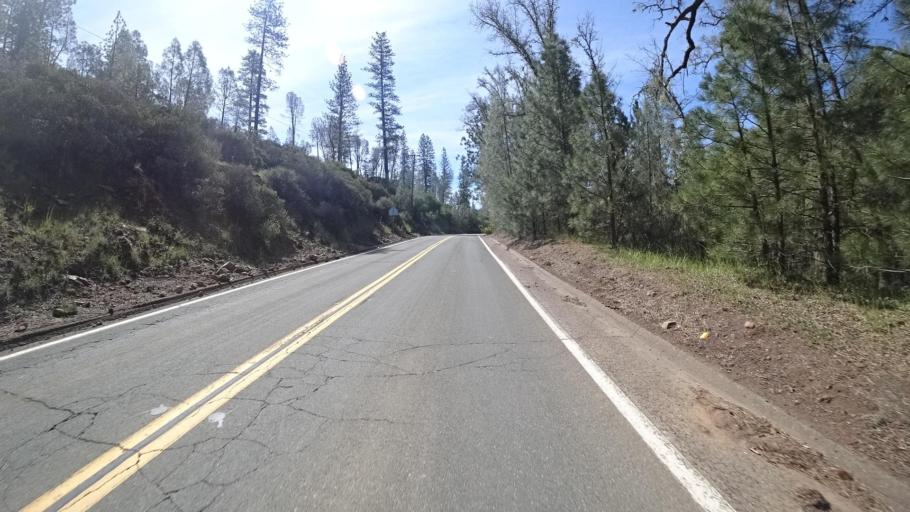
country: US
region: California
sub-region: Lake County
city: Cobb
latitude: 38.8543
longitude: -122.7586
